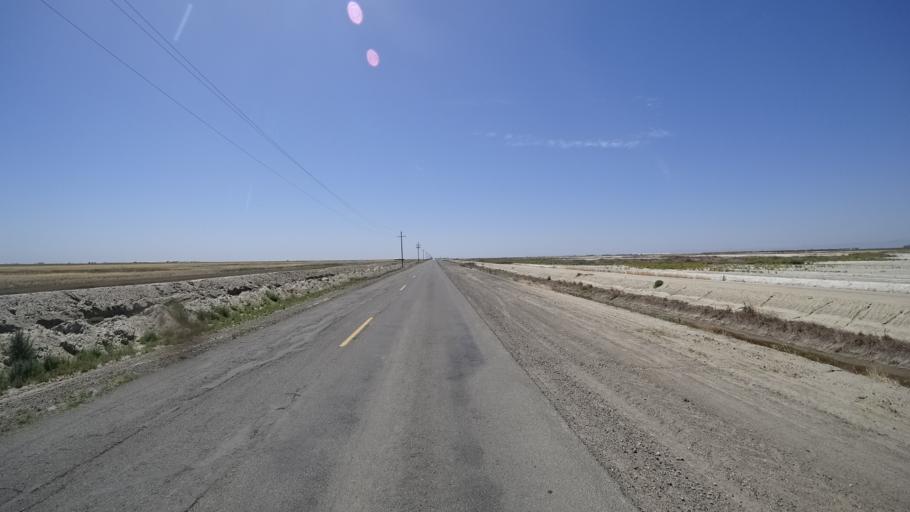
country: US
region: California
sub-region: Kings County
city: Stratford
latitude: 36.1865
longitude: -119.7175
